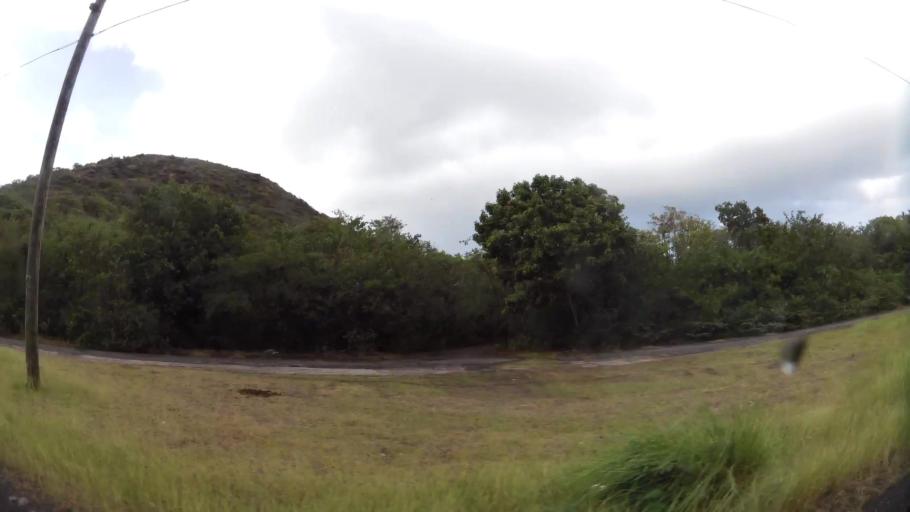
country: KN
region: Saint James Windwa
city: Newcastle
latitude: 17.2030
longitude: -62.6066
